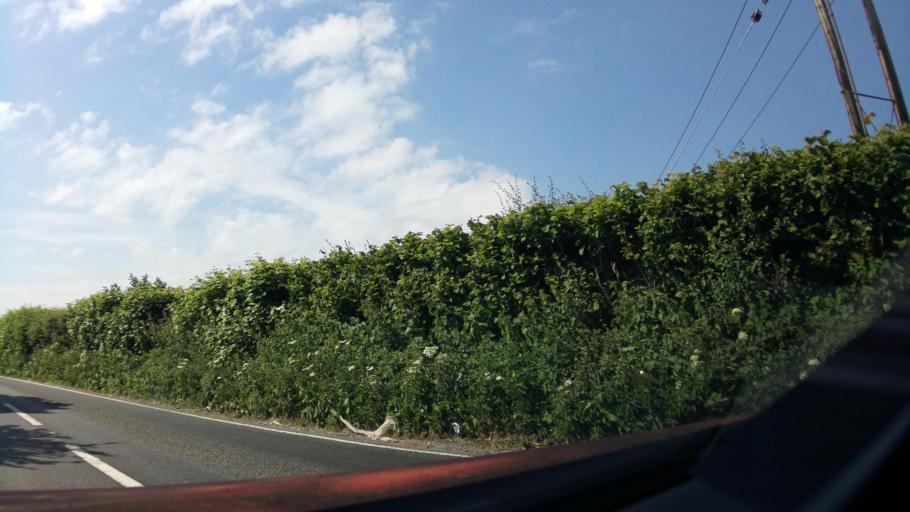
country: GB
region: England
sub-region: Somerset
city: Shepton Mallet
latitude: 51.1974
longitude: -2.5381
